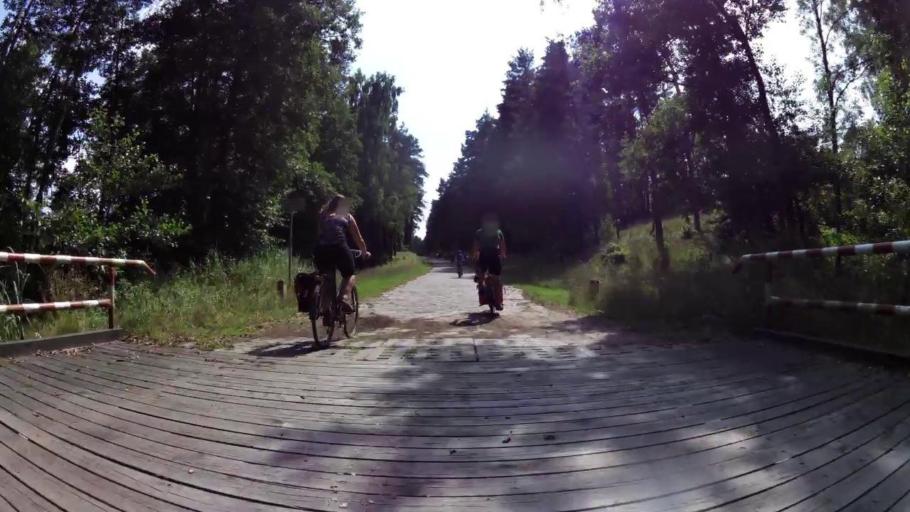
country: PL
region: West Pomeranian Voivodeship
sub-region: Powiat choszczenski
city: Drawno
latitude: 53.3339
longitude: 15.6974
